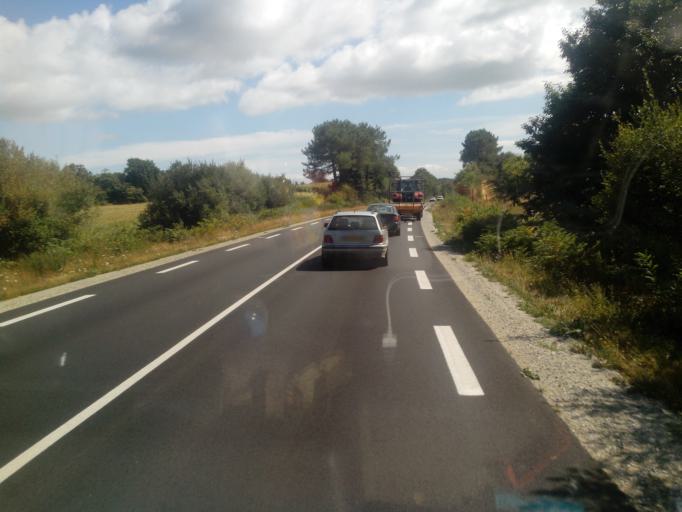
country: FR
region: Brittany
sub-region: Departement du Morbihan
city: Peaule
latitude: 47.6046
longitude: -2.3841
